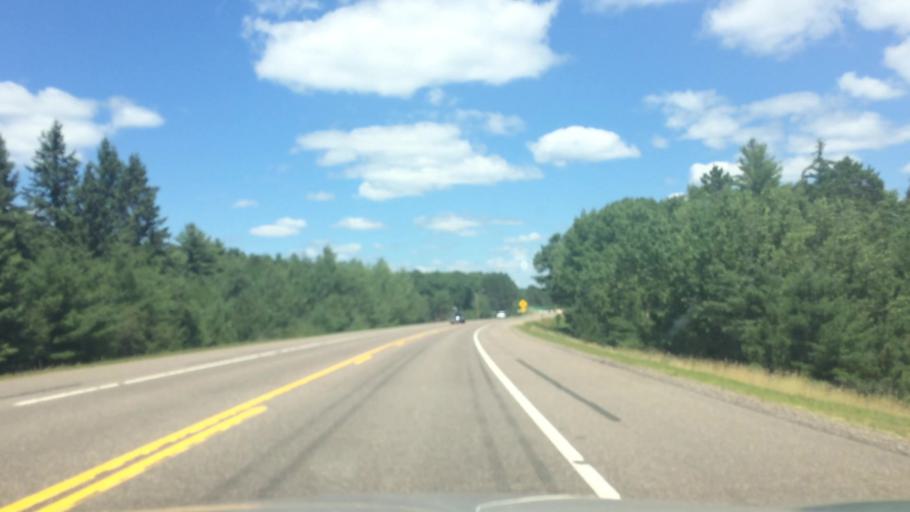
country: US
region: Wisconsin
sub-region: Vilas County
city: Lac du Flambeau
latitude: 45.9495
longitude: -89.7007
